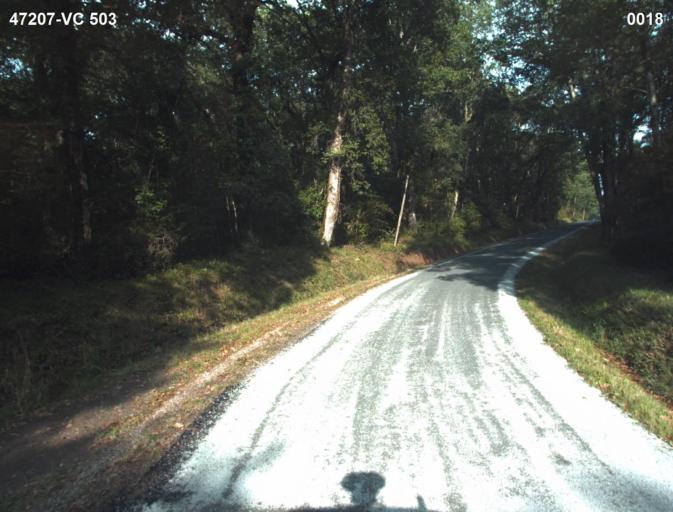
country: FR
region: Aquitaine
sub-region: Departement du Lot-et-Garonne
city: Barbaste
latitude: 44.2060
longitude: 0.2351
